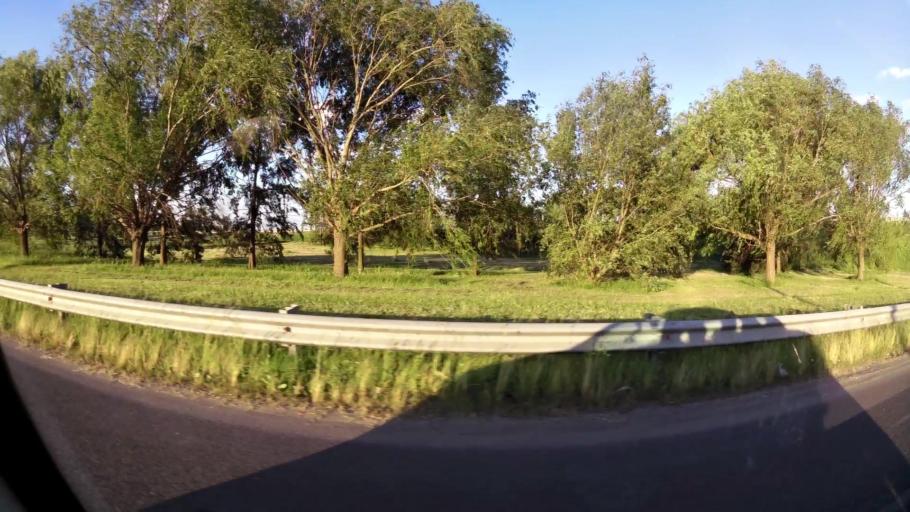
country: AR
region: Buenos Aires
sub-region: Partido de Quilmes
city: Quilmes
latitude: -34.7817
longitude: -58.1531
